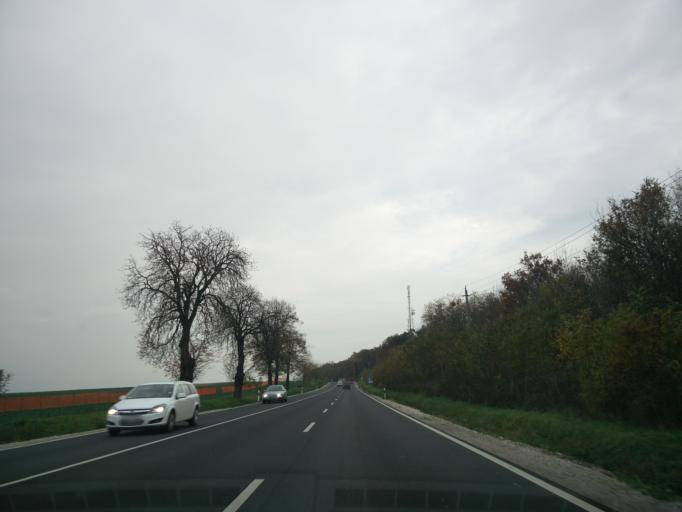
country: HU
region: Somogy
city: Balatonbereny
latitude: 46.6909
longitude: 17.3262
